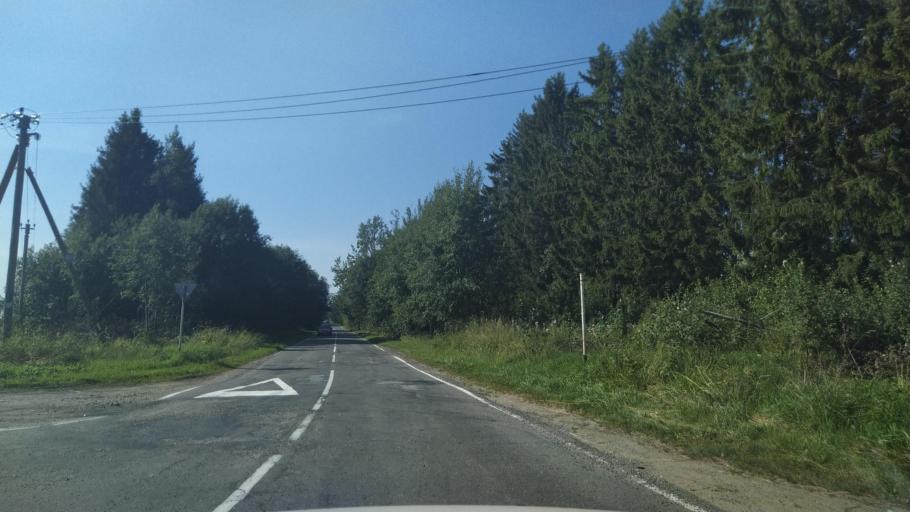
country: RU
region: Leningrad
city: Siverskiy
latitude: 59.3026
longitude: 30.0797
